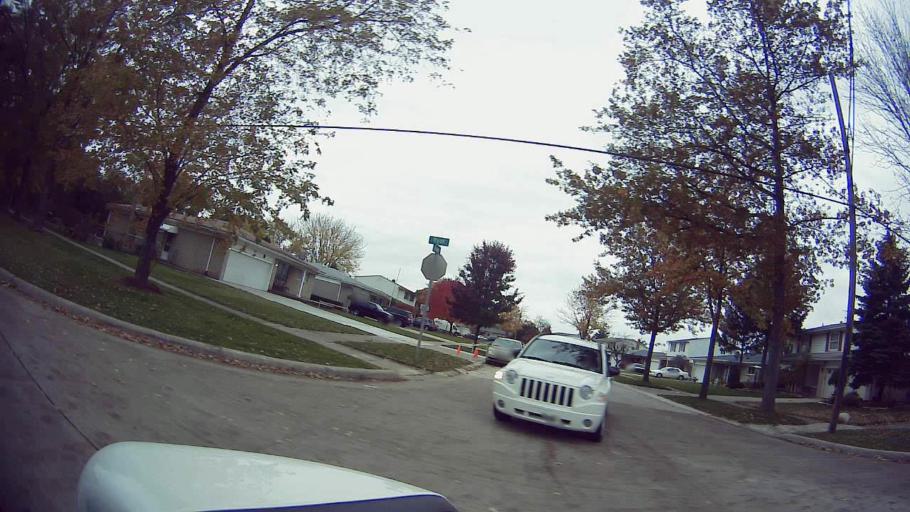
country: US
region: Michigan
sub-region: Macomb County
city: Sterling Heights
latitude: 42.5453
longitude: -83.0691
